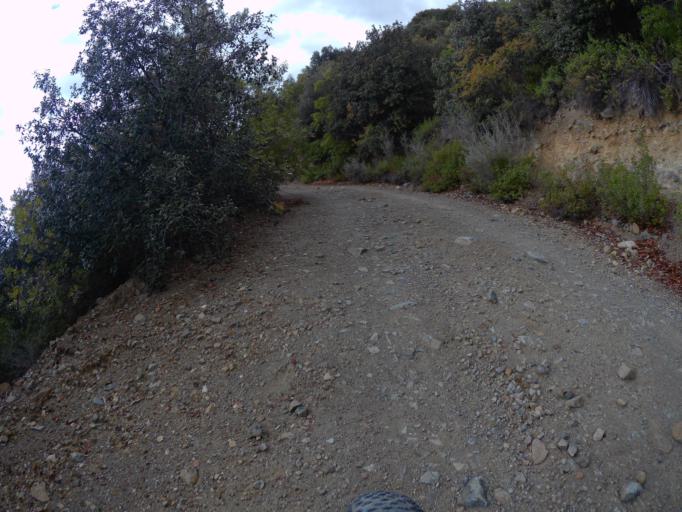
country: CY
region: Lefkosia
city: Kakopetria
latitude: 34.9043
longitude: 32.8314
